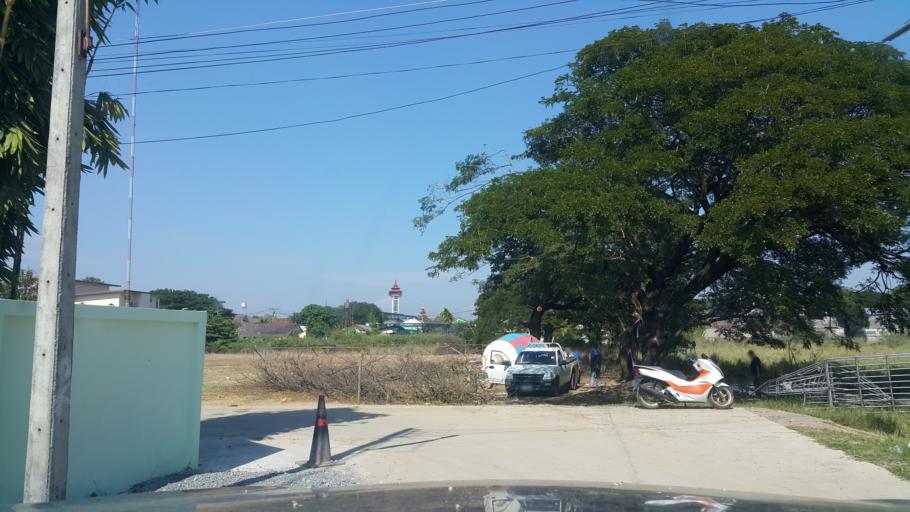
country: TH
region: Chiang Mai
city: Chiang Mai
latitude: 18.7718
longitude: 99.0349
